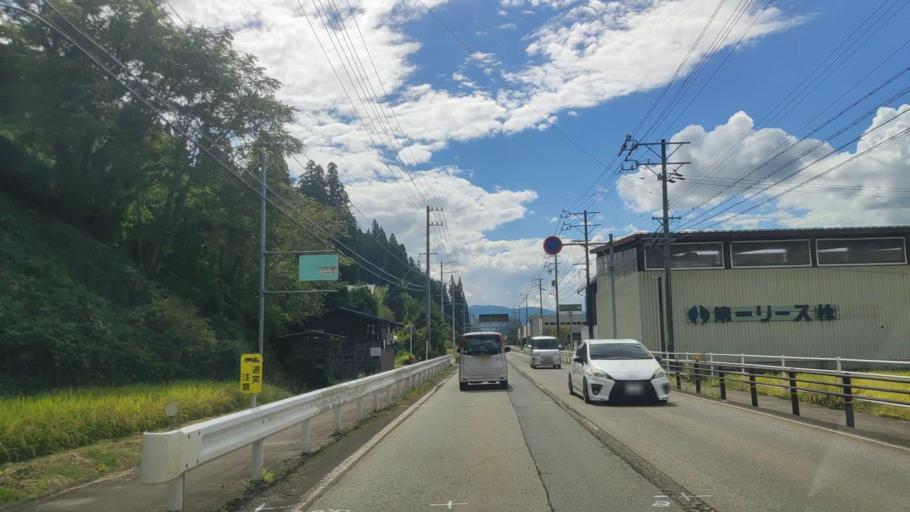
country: JP
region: Gifu
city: Takayama
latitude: 36.1840
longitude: 137.2528
